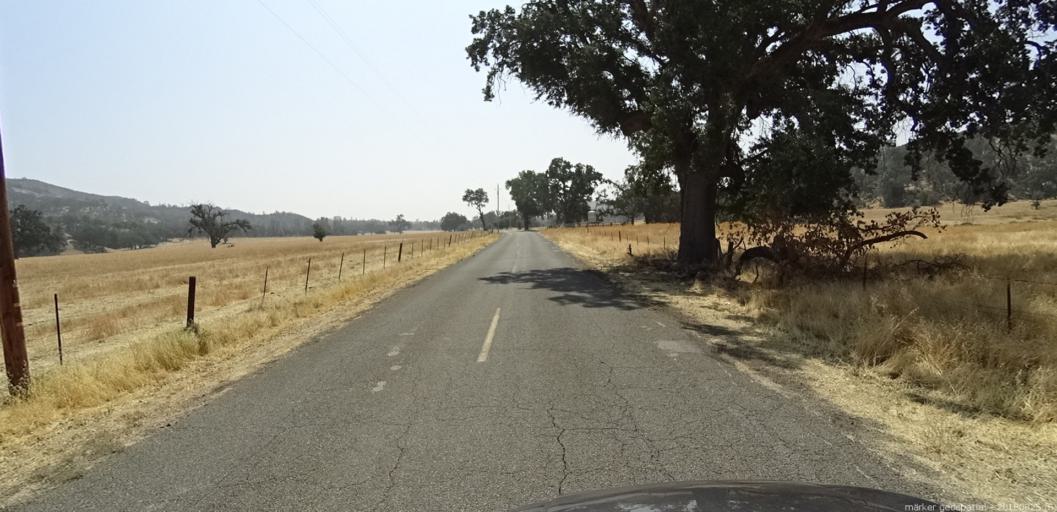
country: US
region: California
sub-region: Fresno County
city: Coalinga
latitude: 35.9250
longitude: -120.5001
